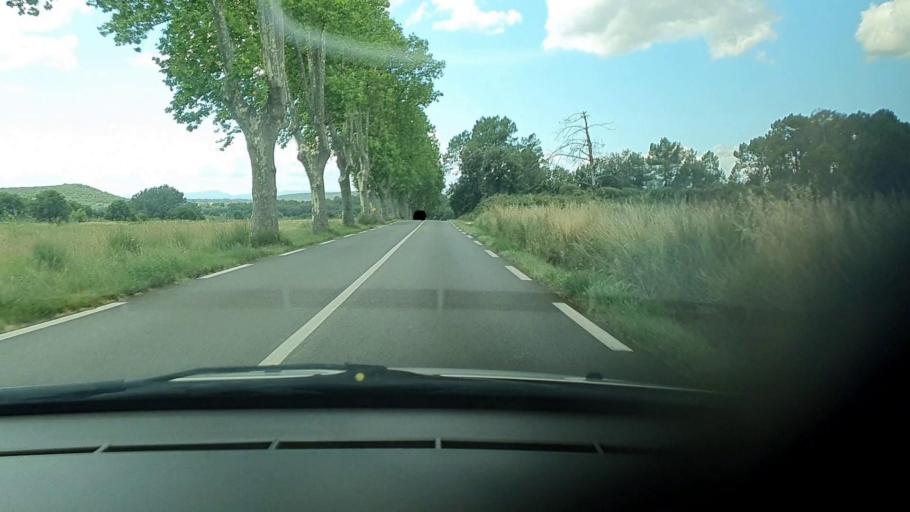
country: FR
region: Languedoc-Roussillon
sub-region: Departement du Gard
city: Montaren-et-Saint-Mediers
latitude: 44.0386
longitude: 4.3201
